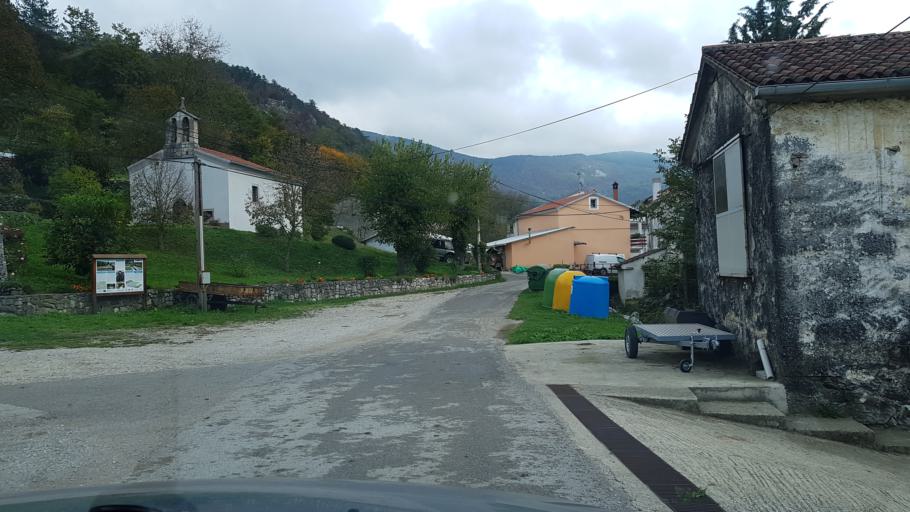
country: HR
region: Istarska
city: Buzet
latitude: 45.4110
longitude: 14.1028
